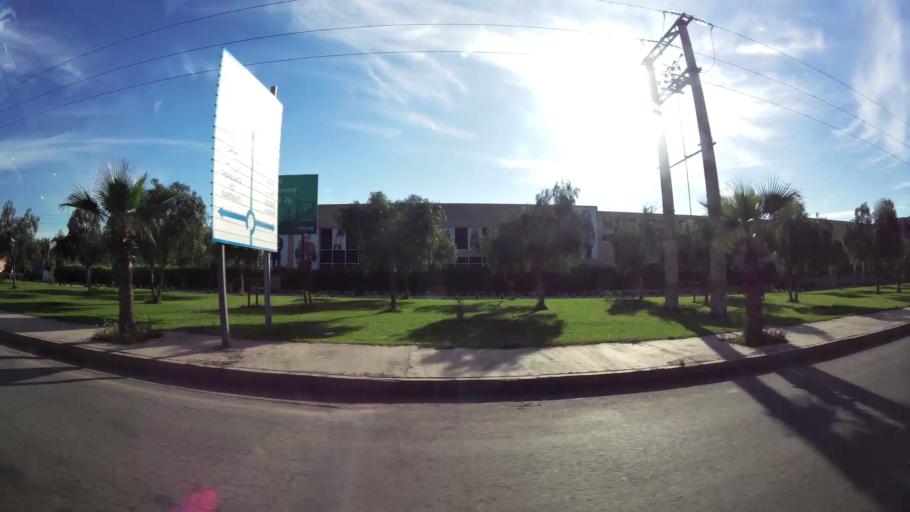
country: MA
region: Marrakech-Tensift-Al Haouz
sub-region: Marrakech
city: Marrakesh
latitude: 31.6829
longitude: -8.0504
